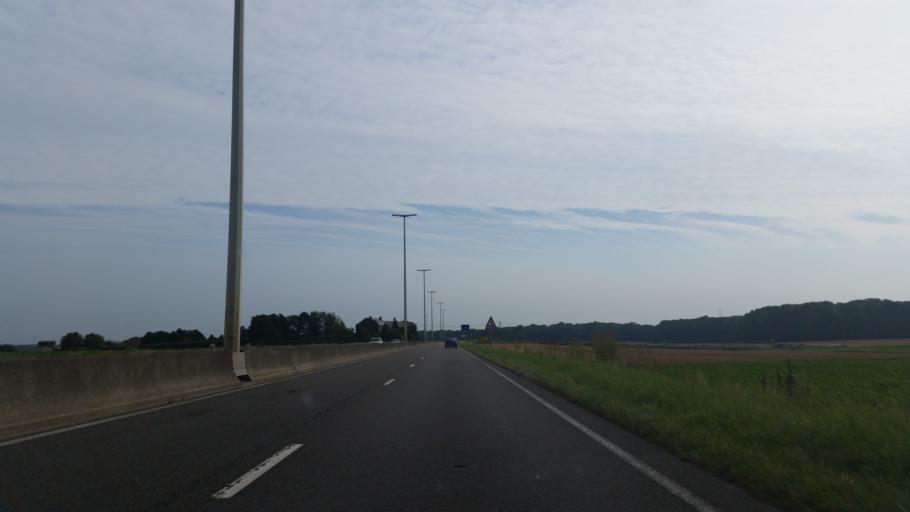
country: BE
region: Wallonia
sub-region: Province de Liege
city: Nandrin
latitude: 50.5279
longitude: 5.4286
